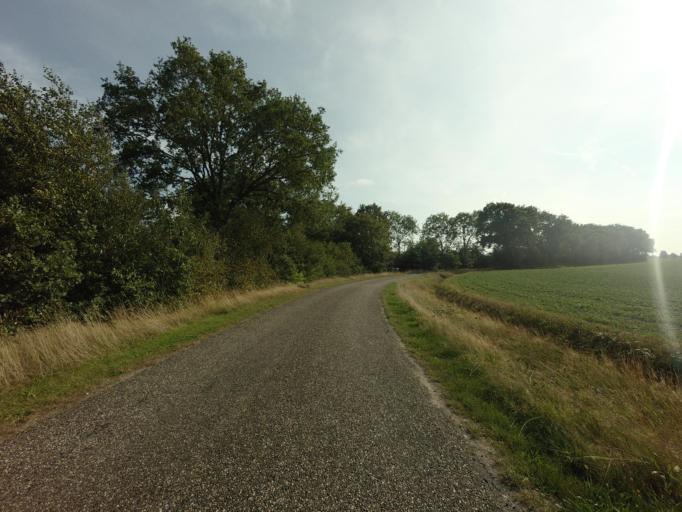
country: NL
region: Drenthe
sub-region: Gemeente Tynaarlo
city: Vries
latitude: 53.1046
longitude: 6.5494
